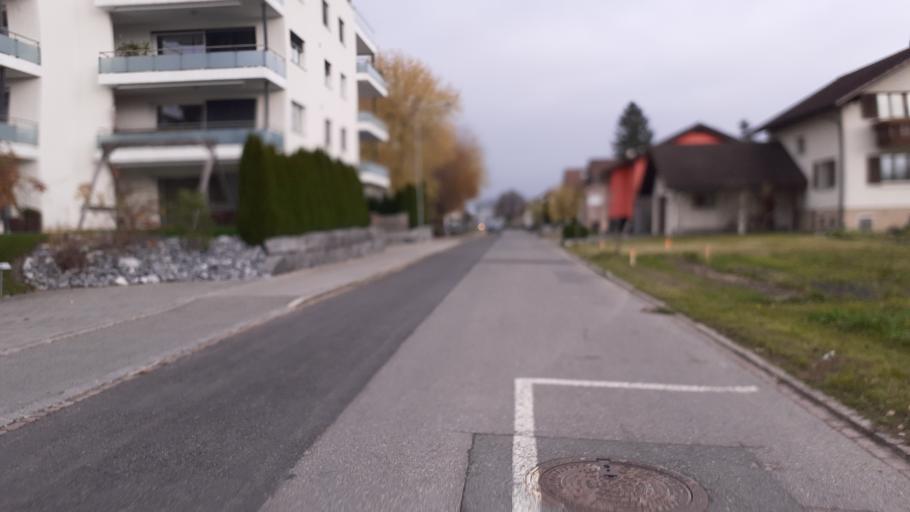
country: CH
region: Saint Gallen
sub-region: Wahlkreis Rheintal
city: Oberriet
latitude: 47.3152
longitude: 9.5672
